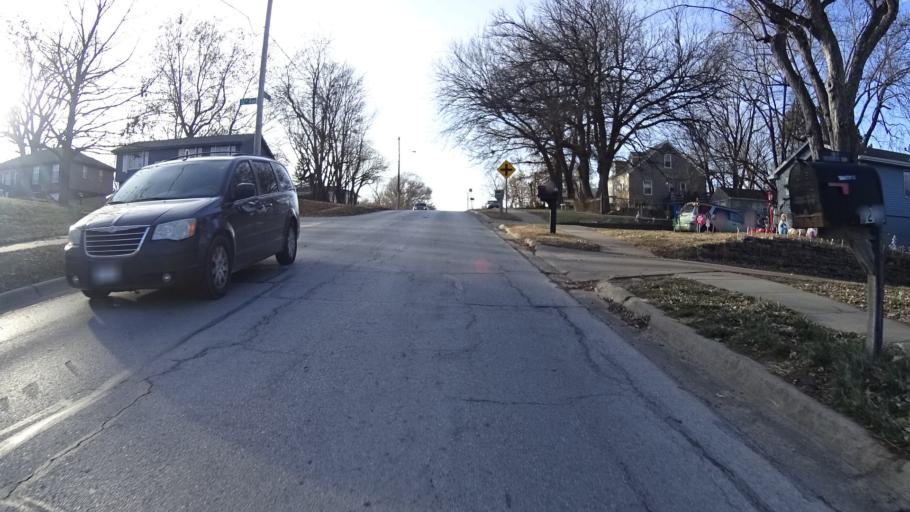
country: US
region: Nebraska
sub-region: Sarpy County
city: La Vista
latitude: 41.1909
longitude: -95.9610
